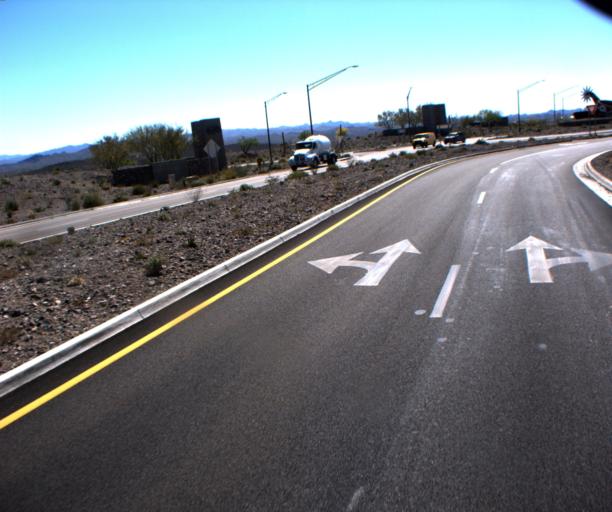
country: US
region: Arizona
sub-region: Maricopa County
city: Wickenburg
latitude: 34.0176
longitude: -112.7989
